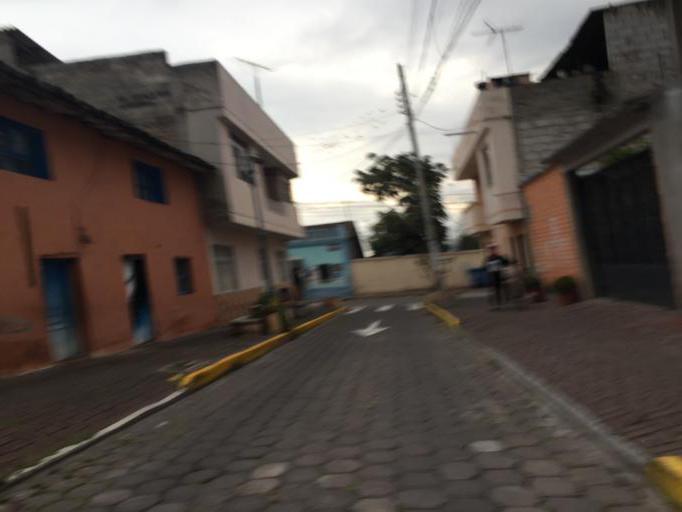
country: EC
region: Imbabura
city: Atuntaqui
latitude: 0.3358
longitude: -78.1711
